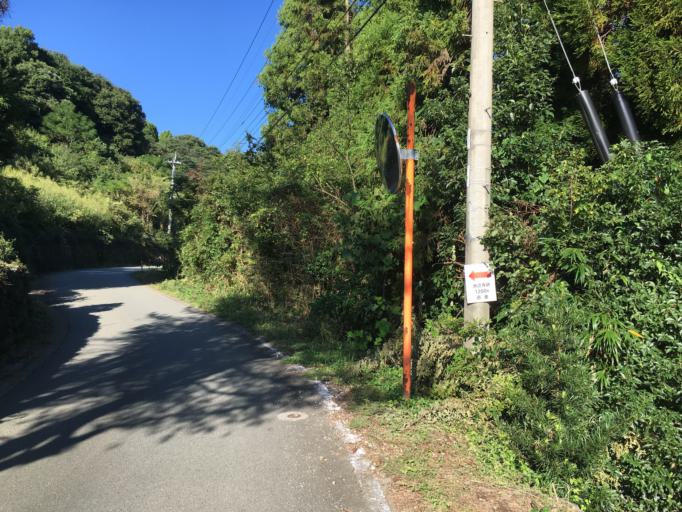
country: JP
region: Kumamoto
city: Kumamoto
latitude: 32.7977
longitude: 130.6650
